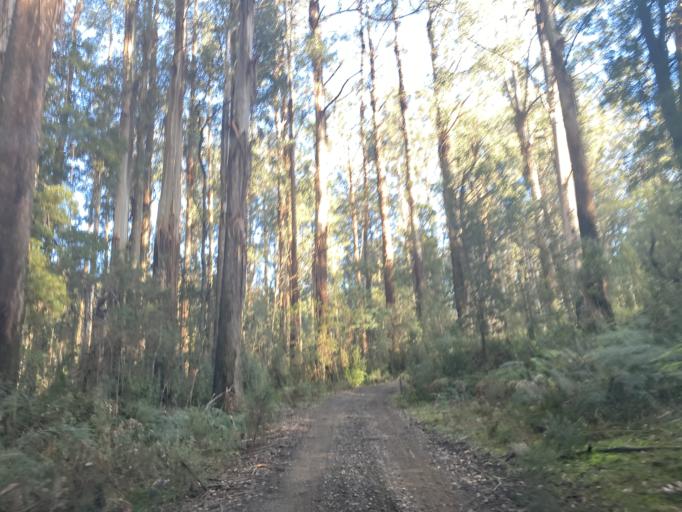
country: AU
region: Victoria
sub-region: Yarra Ranges
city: Healesville
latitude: -37.4790
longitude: 145.5650
